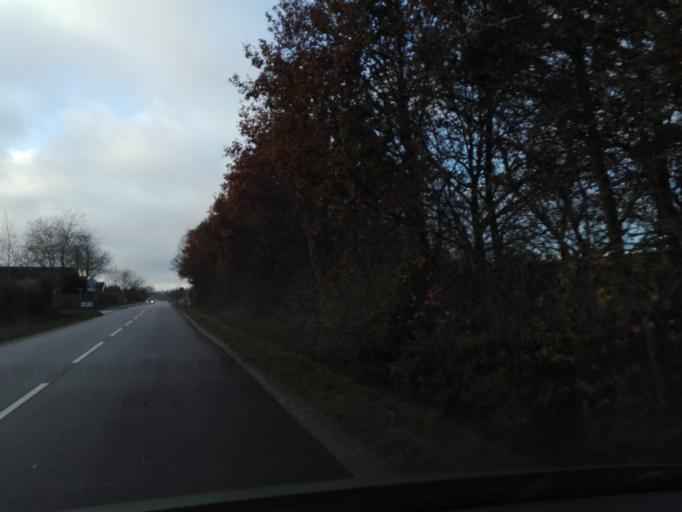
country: DK
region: Central Jutland
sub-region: Arhus Kommune
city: Solbjerg
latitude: 56.0332
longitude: 10.0342
